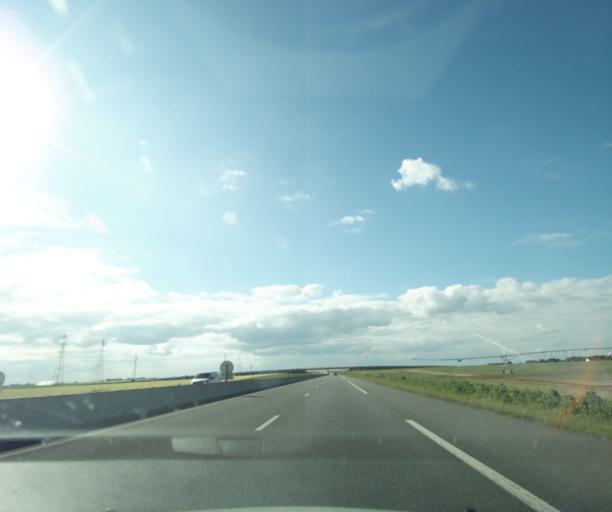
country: FR
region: Centre
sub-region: Departement d'Eure-et-Loir
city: Sours
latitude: 48.3445
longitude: 1.6304
